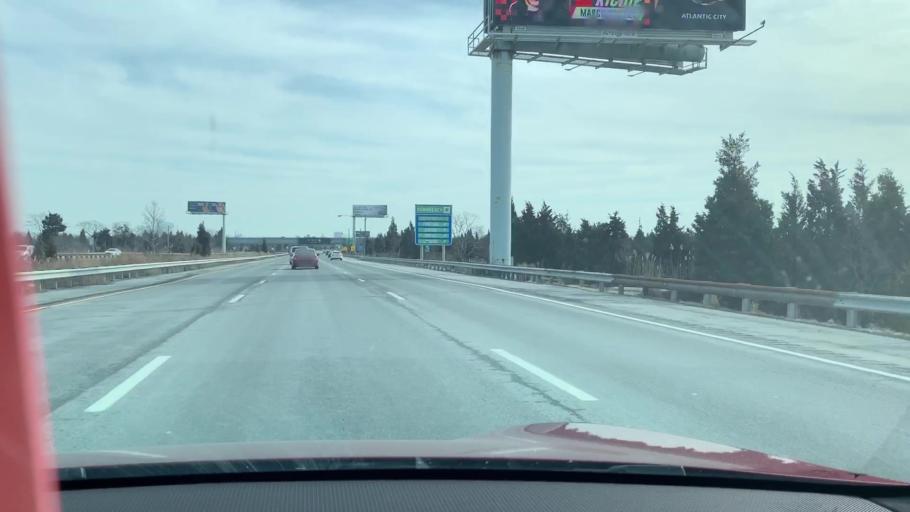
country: US
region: New Jersey
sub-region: Atlantic County
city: Ventnor City
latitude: 39.3788
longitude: -74.4861
